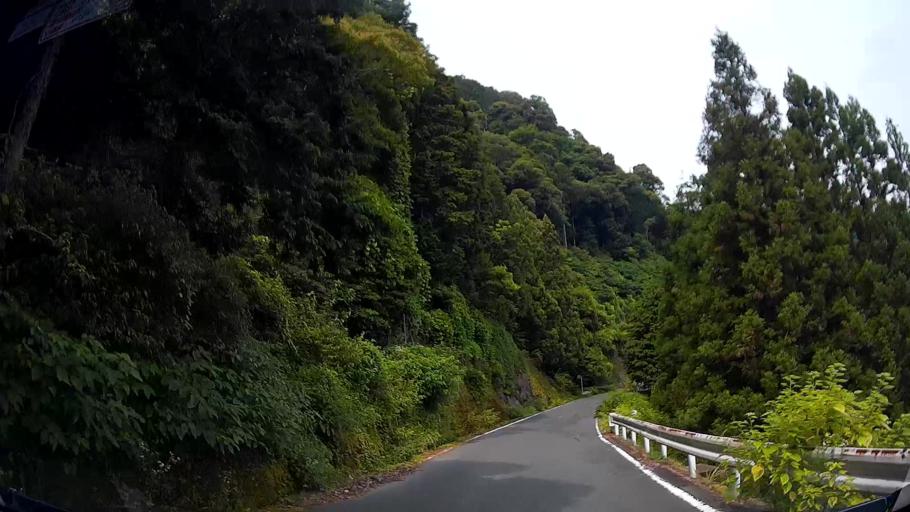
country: JP
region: Shizuoka
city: Hamakita
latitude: 34.9087
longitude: 137.8111
